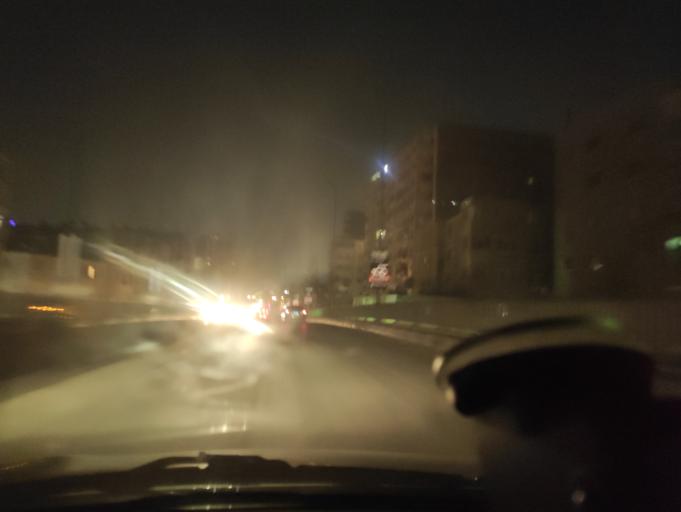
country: EG
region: Muhafazat al Qahirah
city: Cairo
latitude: 30.0926
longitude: 31.2772
